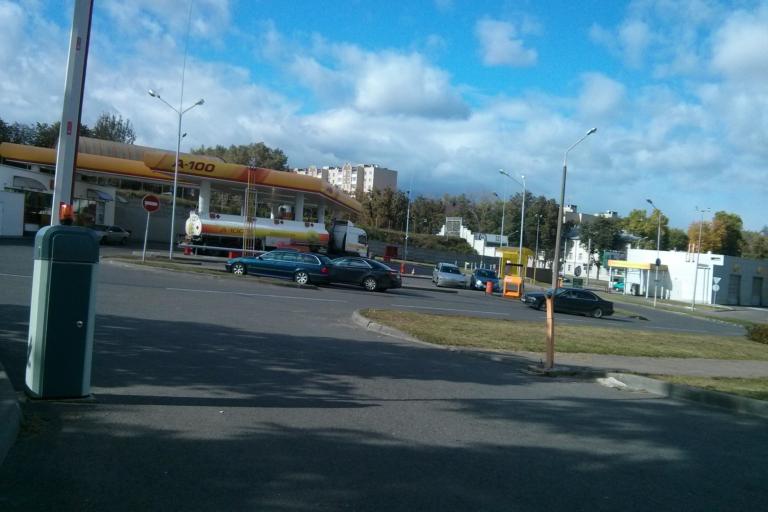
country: BY
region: Minsk
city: Minsk
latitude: 53.8804
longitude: 27.5980
